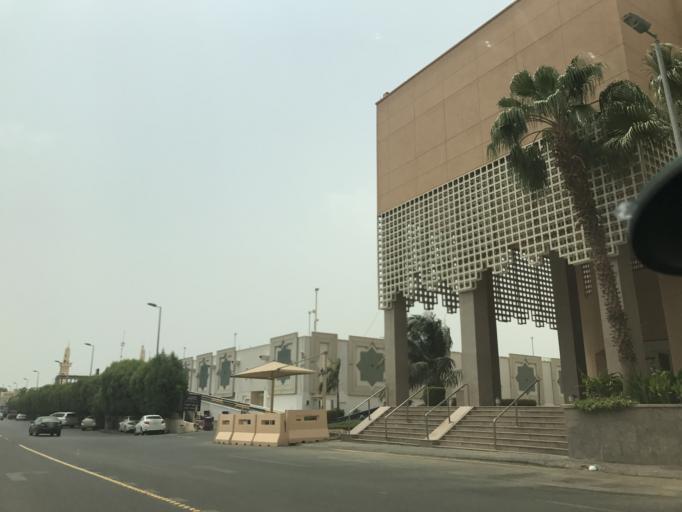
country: SA
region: Makkah
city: Jeddah
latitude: 21.5583
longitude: 39.1723
